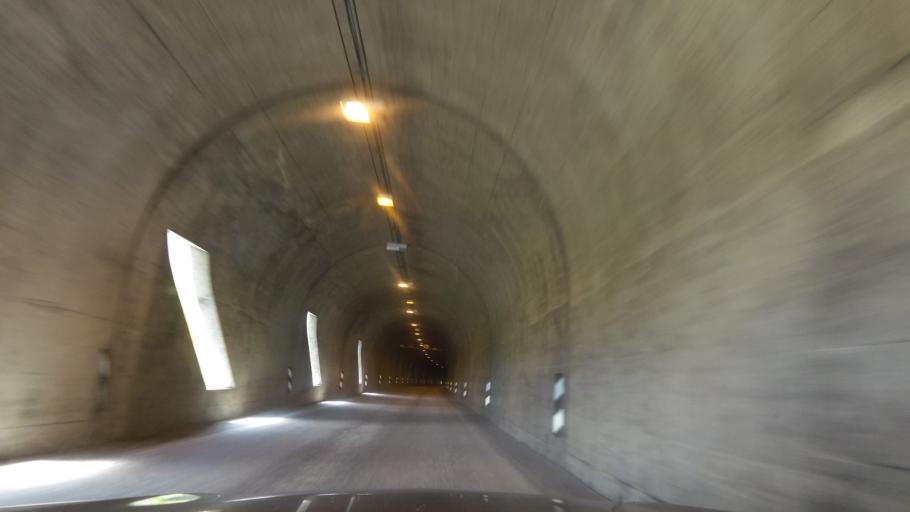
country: IS
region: Westfjords
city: Isafjoerdur
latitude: 66.0291
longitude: -23.3428
